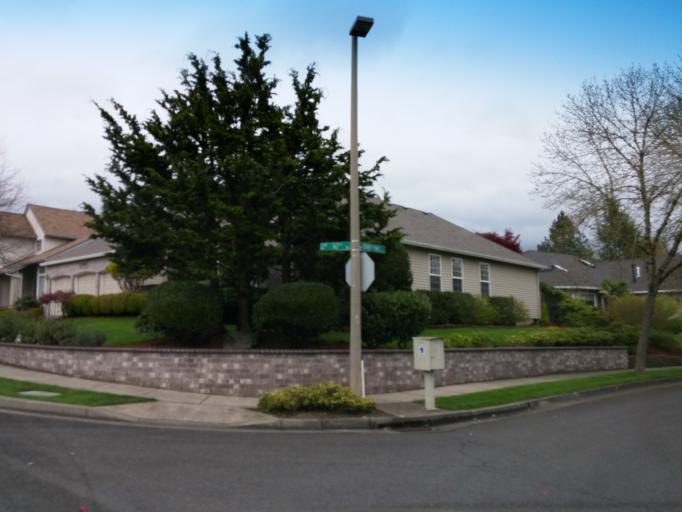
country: US
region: Oregon
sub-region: Washington County
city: Oak Hills
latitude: 45.5223
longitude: -122.8498
